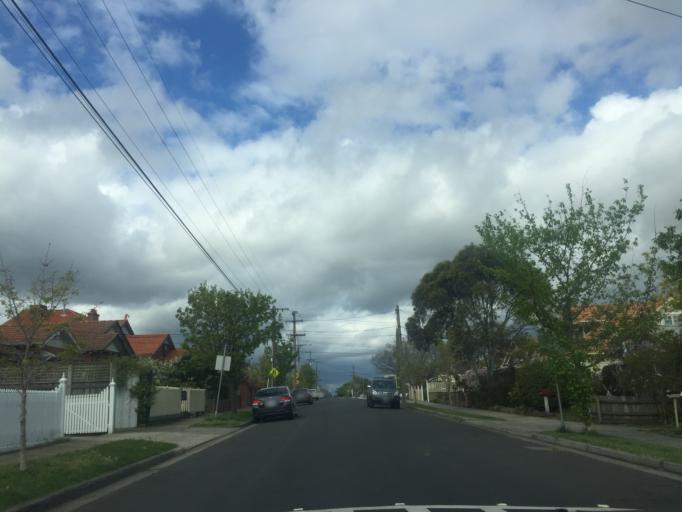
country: AU
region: Victoria
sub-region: Darebin
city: Reservoir
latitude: -37.7275
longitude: 145.0111
